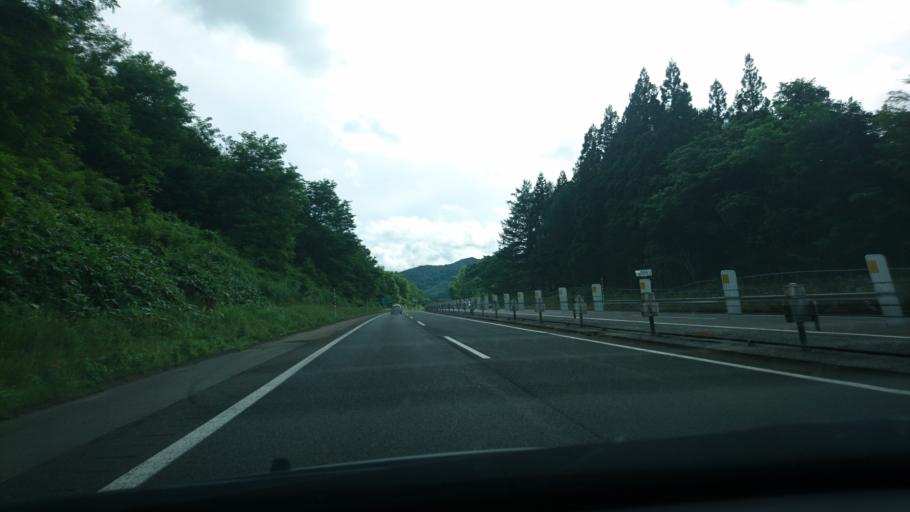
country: JP
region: Akita
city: Hanawa
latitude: 40.0492
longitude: 141.0090
